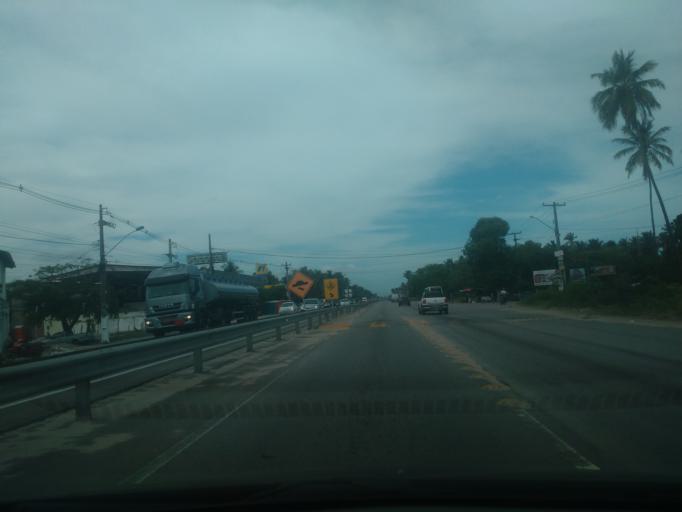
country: BR
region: Alagoas
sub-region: Marechal Deodoro
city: Marechal Deodoro
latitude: -9.7128
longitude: -35.8224
